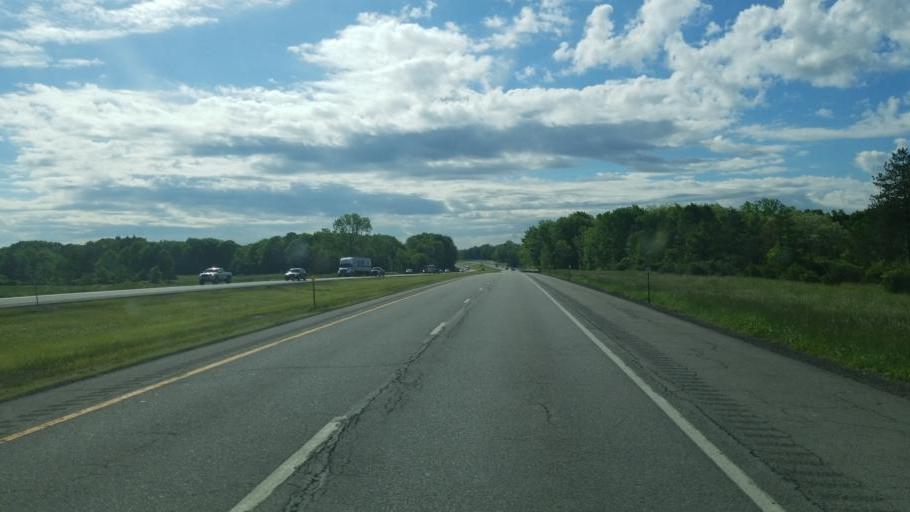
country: US
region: New York
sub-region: Monroe County
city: Pittsford
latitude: 43.0197
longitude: -77.4923
